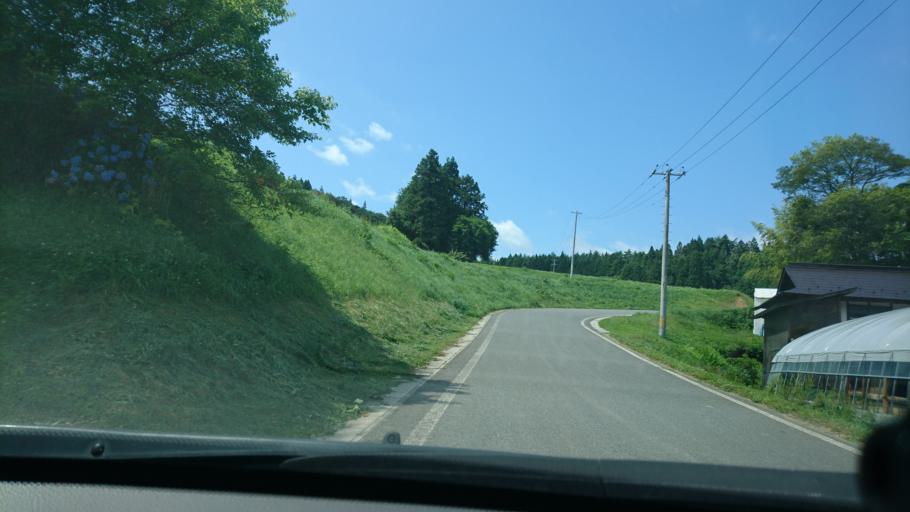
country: JP
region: Iwate
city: Ichinoseki
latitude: 38.9788
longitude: 141.1957
